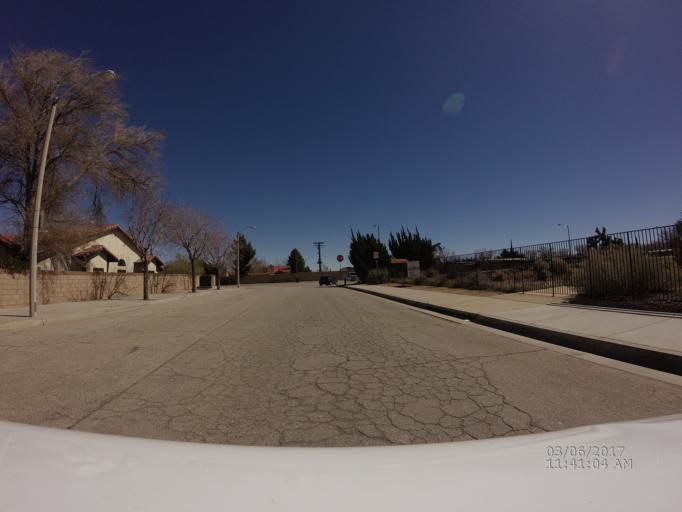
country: US
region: California
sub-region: Los Angeles County
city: Quartz Hill
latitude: 34.6493
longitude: -118.2368
